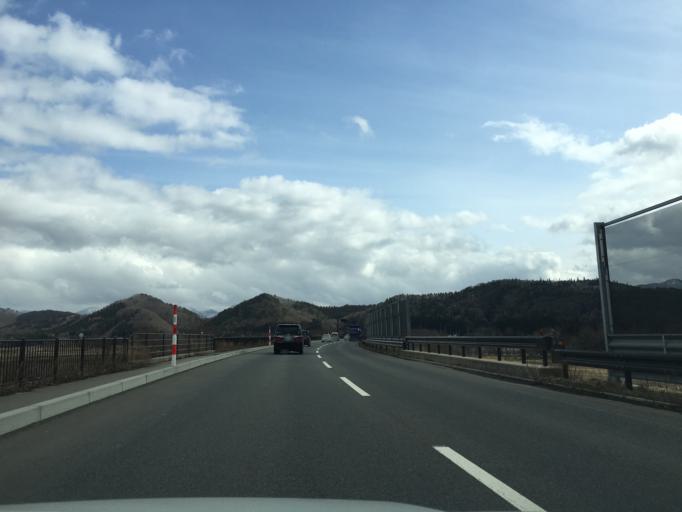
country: JP
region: Akita
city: Hanawa
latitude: 40.2278
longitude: 140.7123
